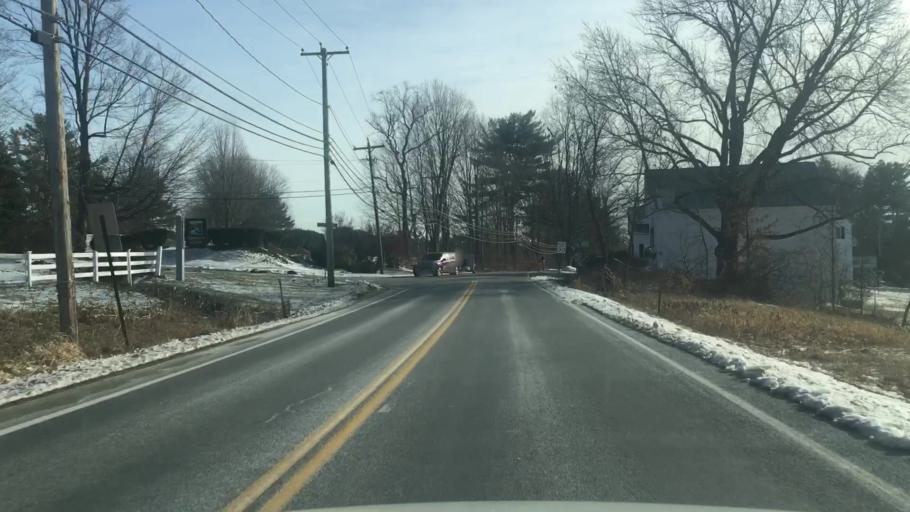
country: US
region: New Hampshire
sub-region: Merrimack County
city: East Concord
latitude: 43.2578
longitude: -71.5450
